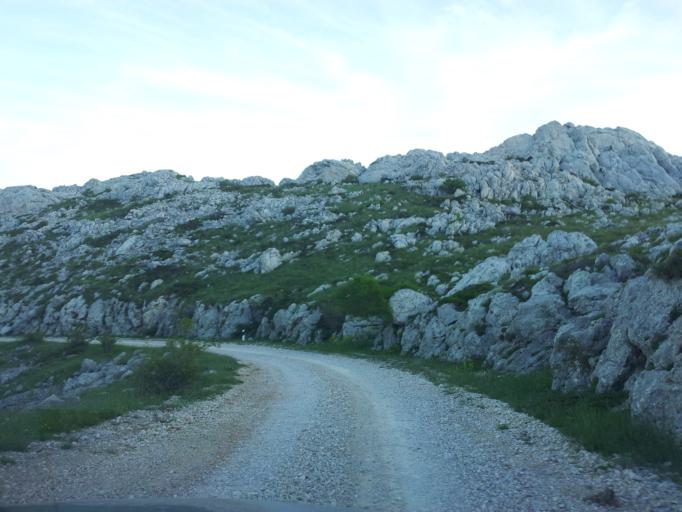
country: HR
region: Zadarska
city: Obrovac
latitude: 44.2650
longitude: 15.6419
